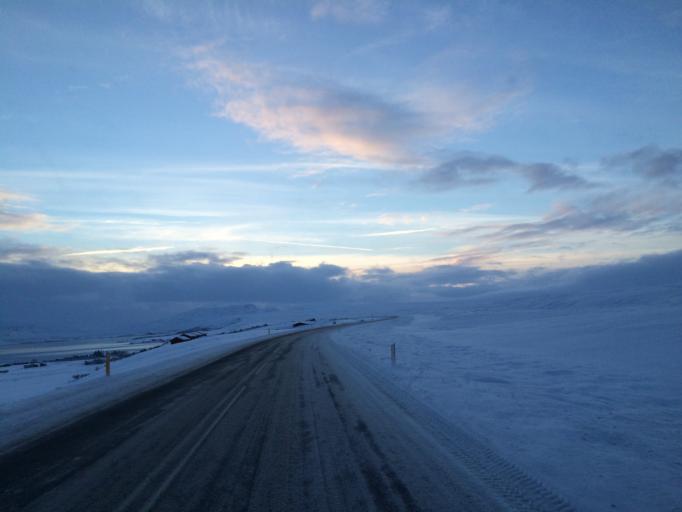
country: IS
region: South
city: Hveragerdi
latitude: 64.2368
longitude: -21.1915
